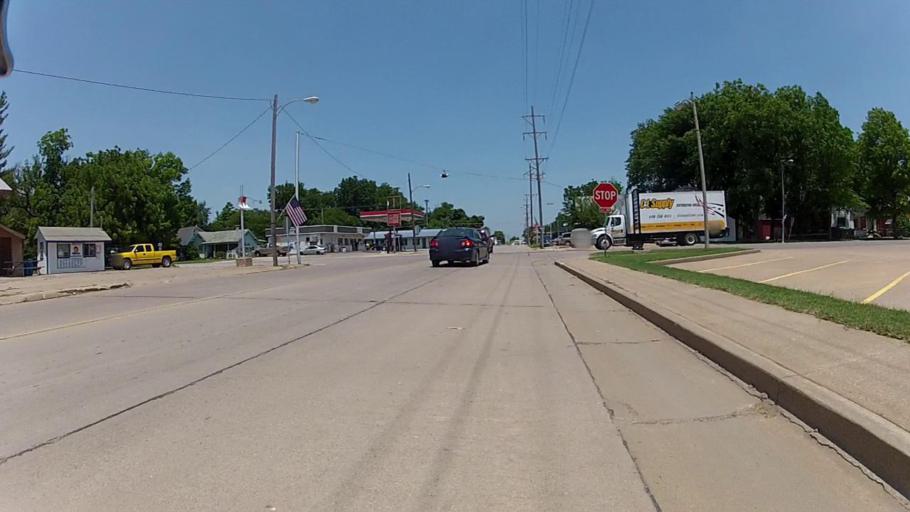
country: US
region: Kansas
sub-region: Montgomery County
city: Cherryvale
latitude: 37.2686
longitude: -95.5557
